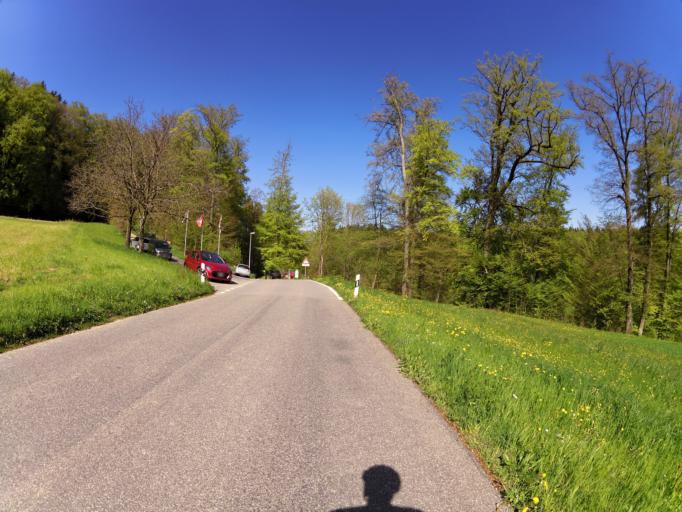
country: CH
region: Aargau
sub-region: Bezirk Aarau
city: Aarau
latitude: 47.3785
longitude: 8.0277
